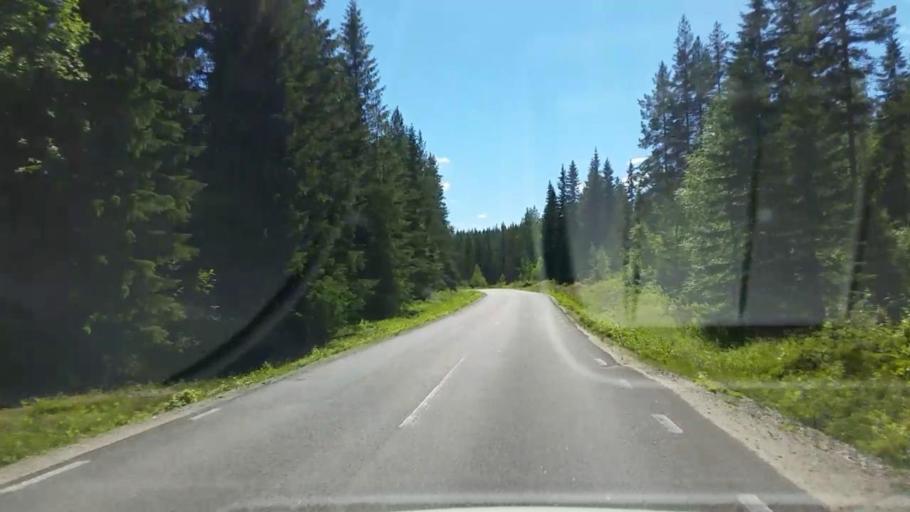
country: SE
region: Gaevleborg
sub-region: Ljusdals Kommun
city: Farila
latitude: 61.6515
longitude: 15.5898
